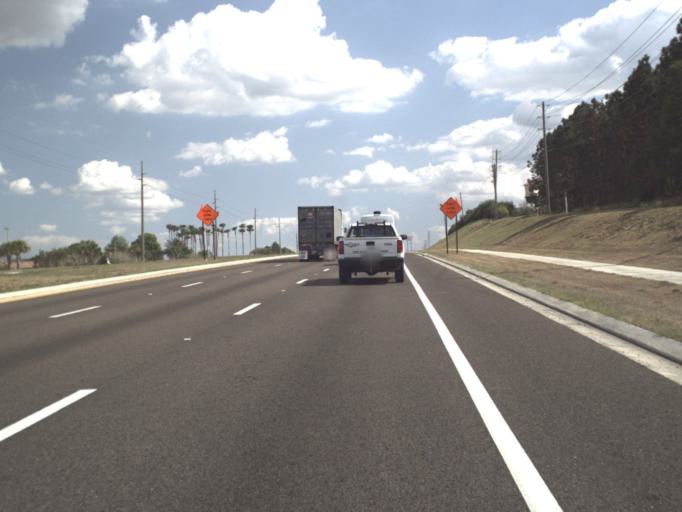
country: US
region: Florida
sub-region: Lake County
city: Clermont
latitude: 28.5126
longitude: -81.7247
